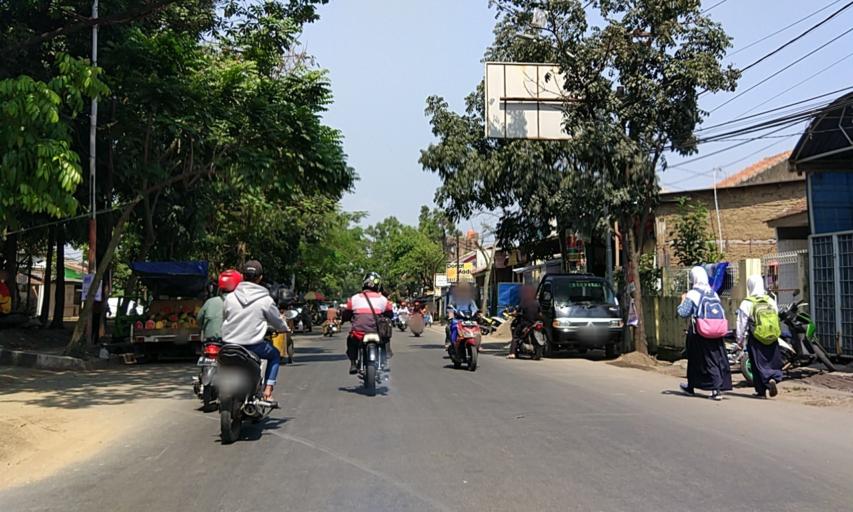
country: ID
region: West Java
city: Margahayukencana
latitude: -6.9201
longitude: 107.5631
